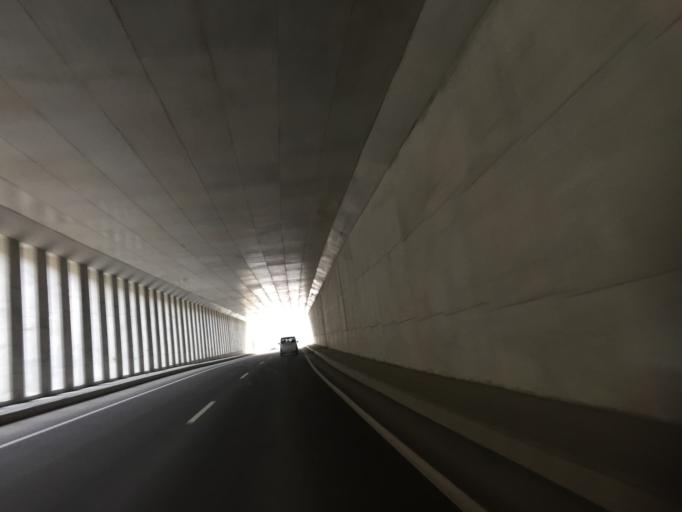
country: TR
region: Trabzon
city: Macka
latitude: 40.7740
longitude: 39.5671
